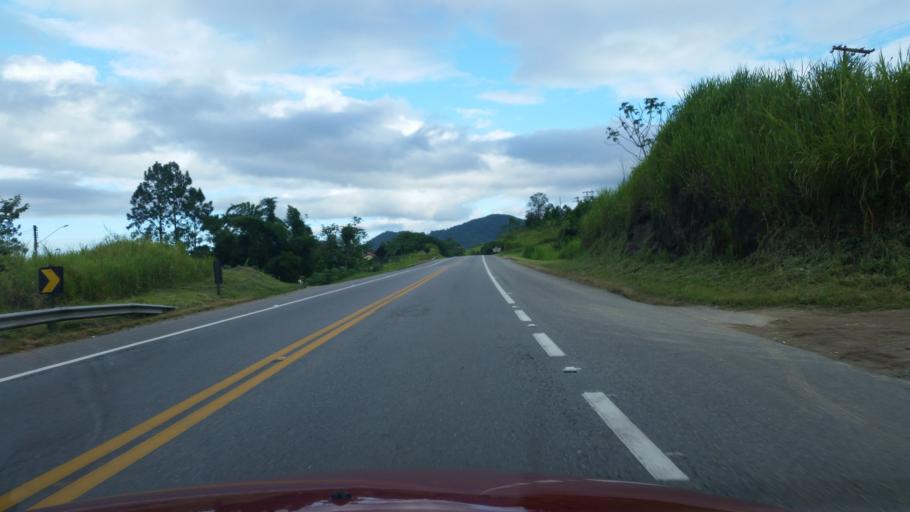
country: BR
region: Sao Paulo
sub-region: Miracatu
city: Miracatu
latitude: -24.2773
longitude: -47.2451
